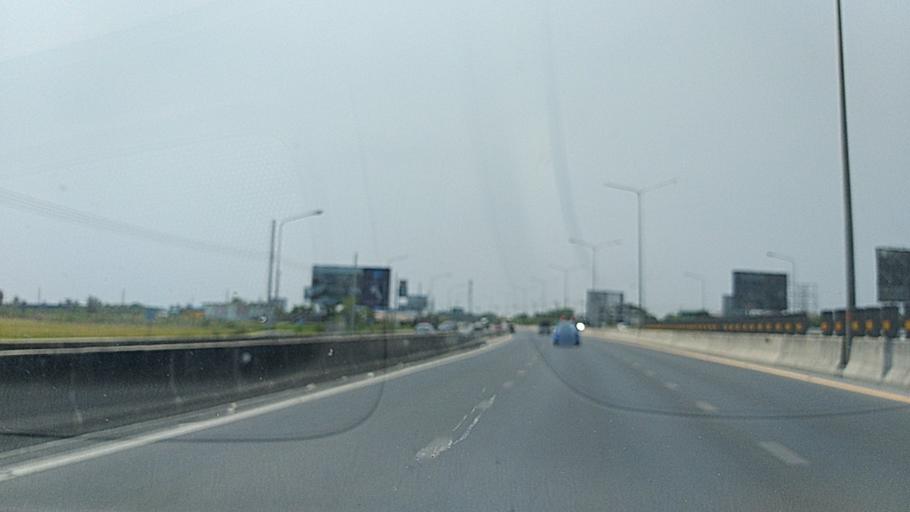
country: TH
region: Nonthaburi
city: Bang Bua Thong
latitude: 13.9293
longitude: 100.4462
